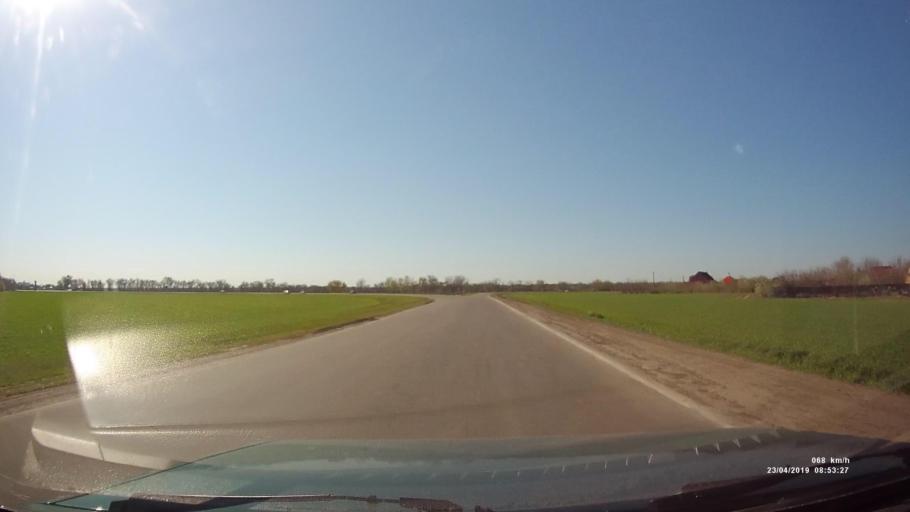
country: RU
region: Rostov
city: Sal'sk
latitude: 46.4754
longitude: 41.4744
